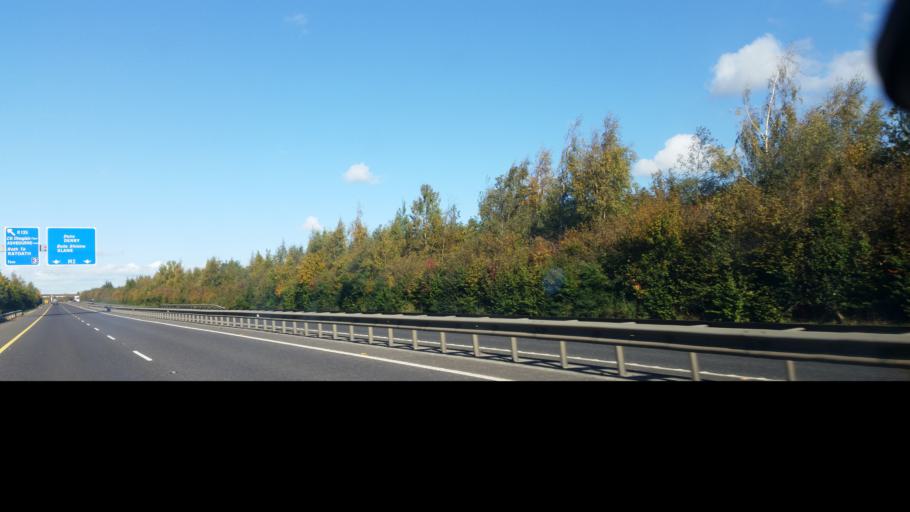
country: IE
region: Leinster
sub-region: An Mhi
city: Ashbourne
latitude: 53.4755
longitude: -6.3689
